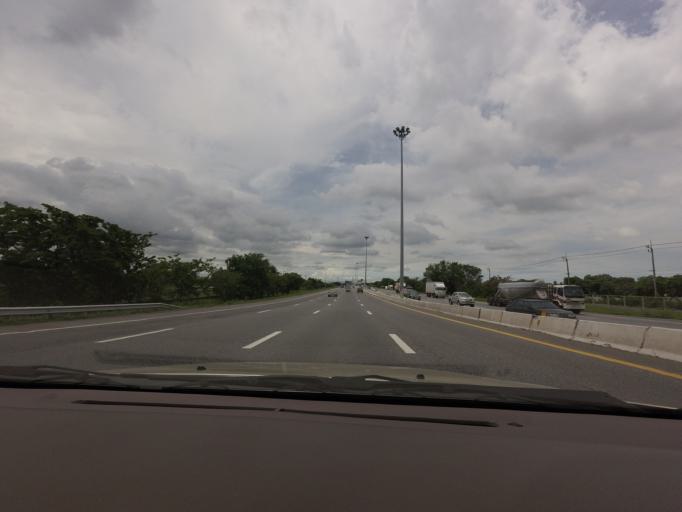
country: TH
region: Samut Prakan
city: Ban Khlong Bang Sao Thong
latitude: 13.6871
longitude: 100.8315
